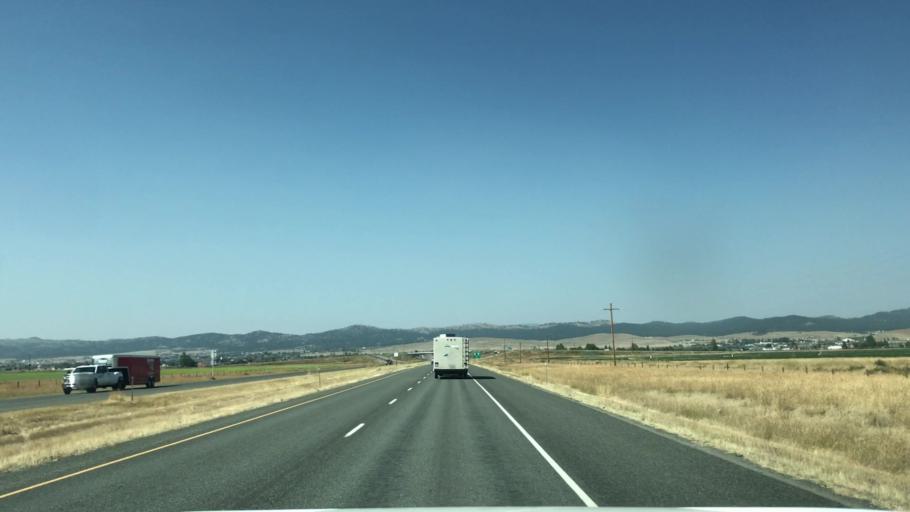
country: US
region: Montana
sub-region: Lewis and Clark County
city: Helena Valley West Central
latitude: 46.6965
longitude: -112.0117
